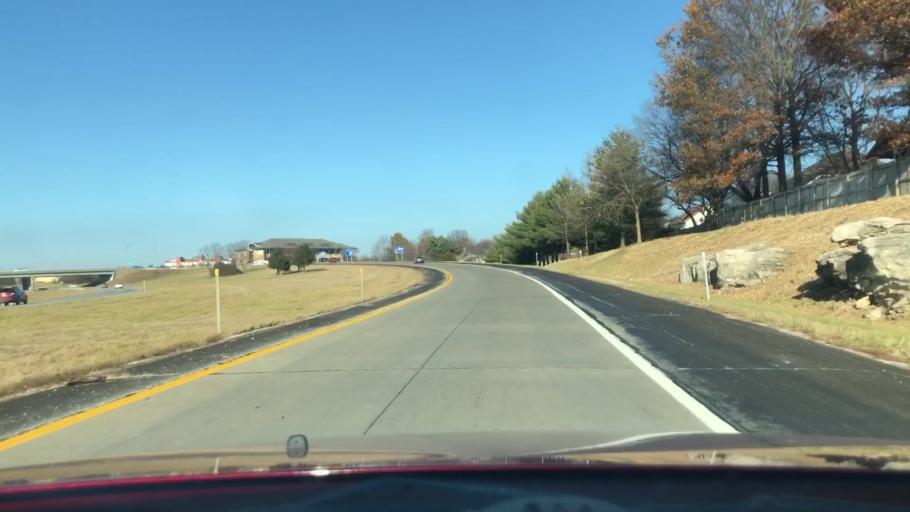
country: US
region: Missouri
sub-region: Greene County
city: Battlefield
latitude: 37.1414
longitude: -93.3151
